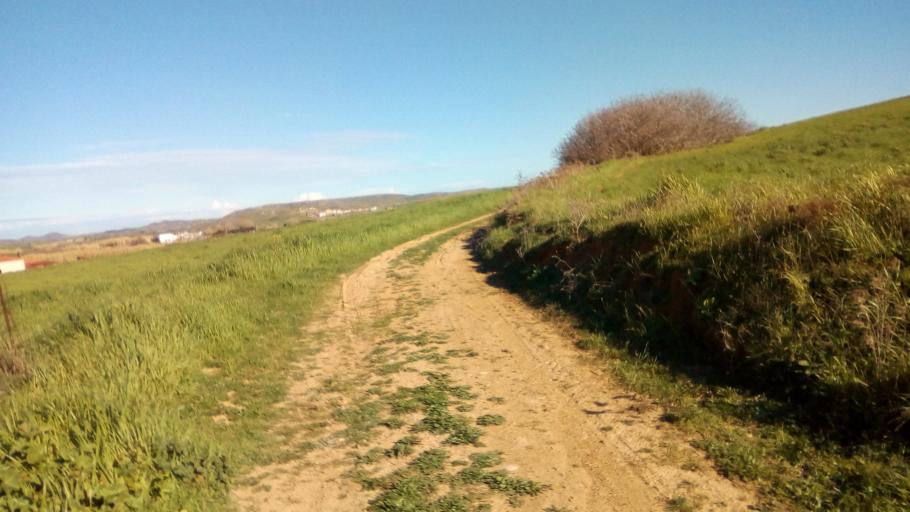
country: GR
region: North Aegean
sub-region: Nomos Lesvou
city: Myrina
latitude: 39.9325
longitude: 25.2351
